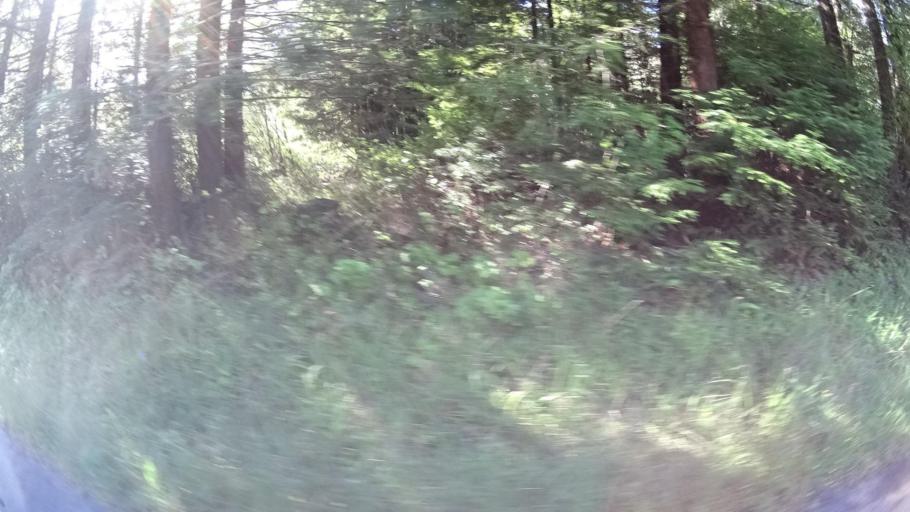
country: US
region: California
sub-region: Humboldt County
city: Rio Dell
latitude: 40.4341
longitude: -123.9669
